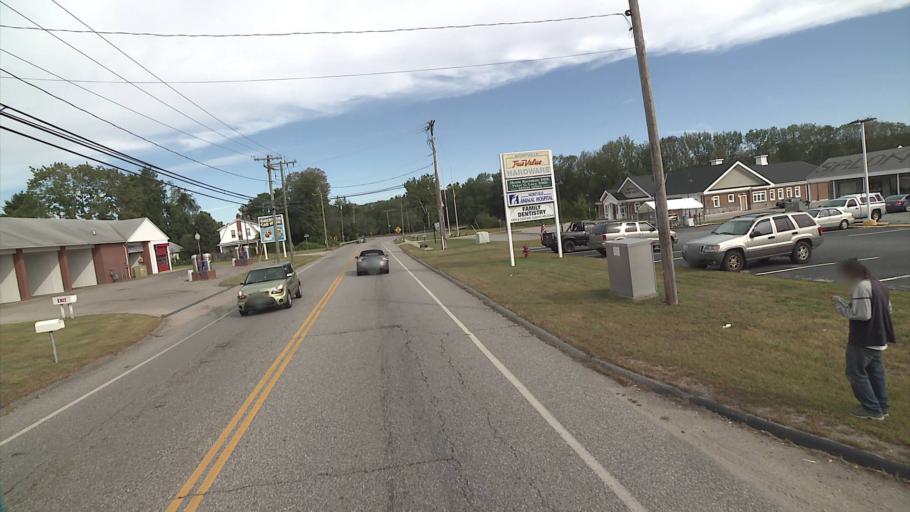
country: US
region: Connecticut
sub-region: New London County
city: Uncasville
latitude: 41.4504
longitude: -72.1067
